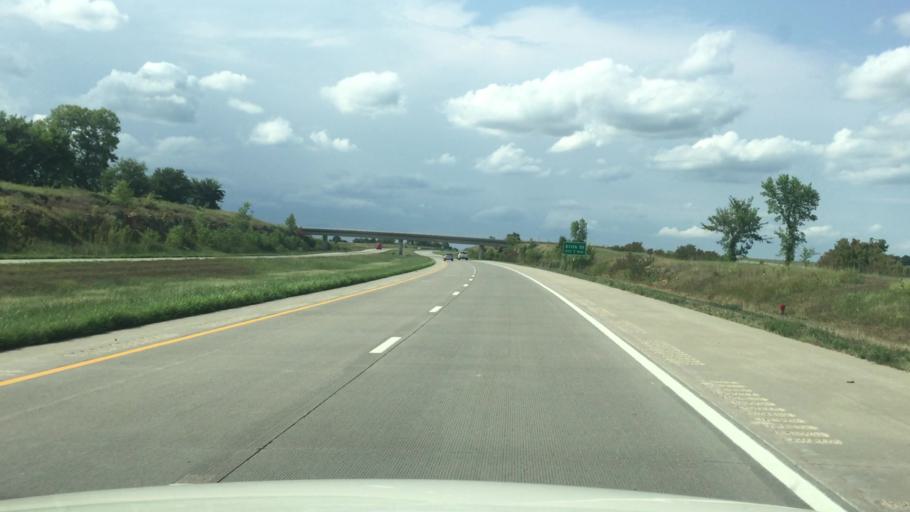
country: US
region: Kansas
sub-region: Miami County
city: Louisburg
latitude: 38.5461
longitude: -94.6859
